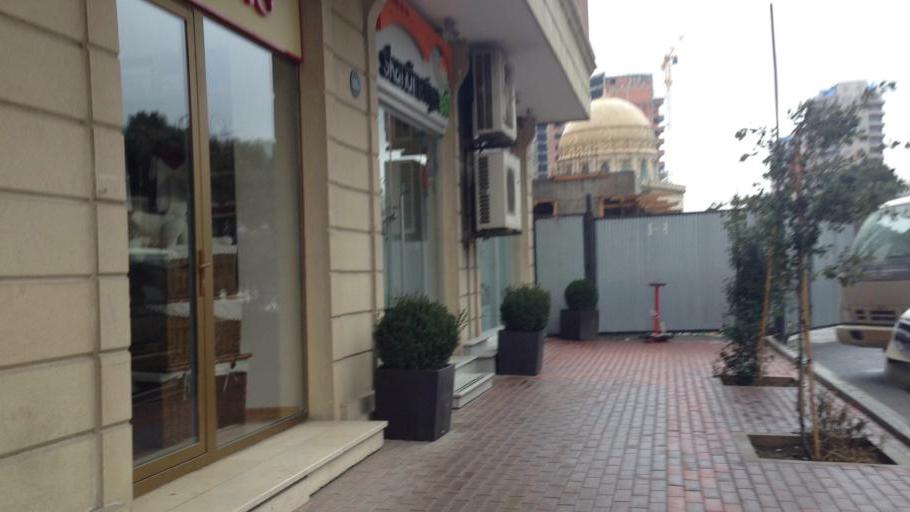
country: AZ
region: Baki
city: Baku
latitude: 40.3869
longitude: 49.8371
